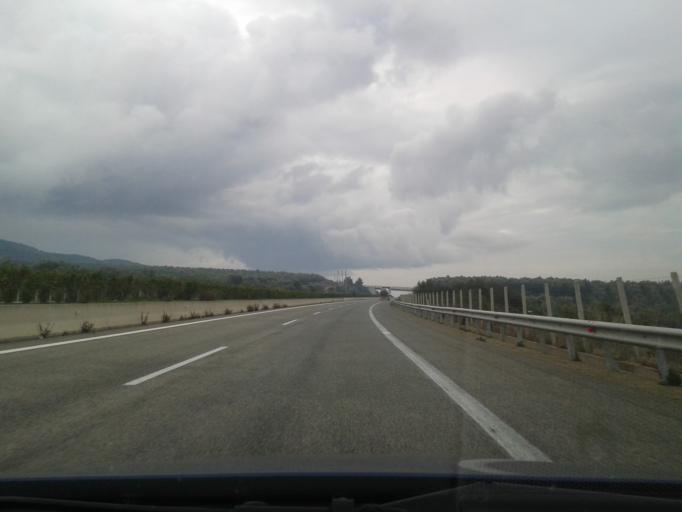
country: GR
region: West Greece
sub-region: Nomos Aitolias kai Akarnanias
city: Angelokastro
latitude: 38.5237
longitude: 21.3007
